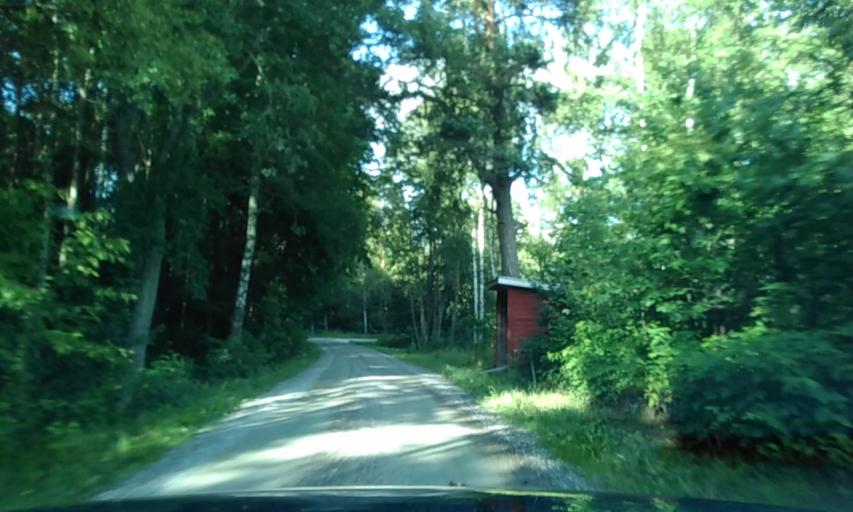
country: SE
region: Vaestra Goetaland
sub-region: Vara Kommun
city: Vara
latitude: 58.3686
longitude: 12.8539
